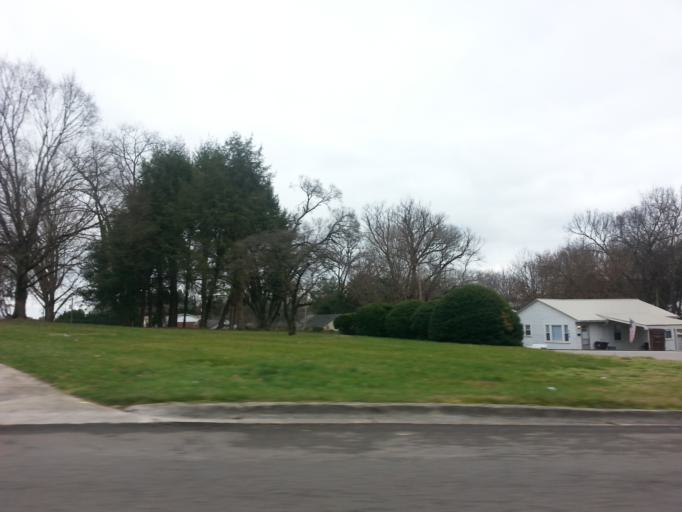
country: US
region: Tennessee
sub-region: Jefferson County
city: Jefferson City
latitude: 36.1186
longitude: -83.4925
